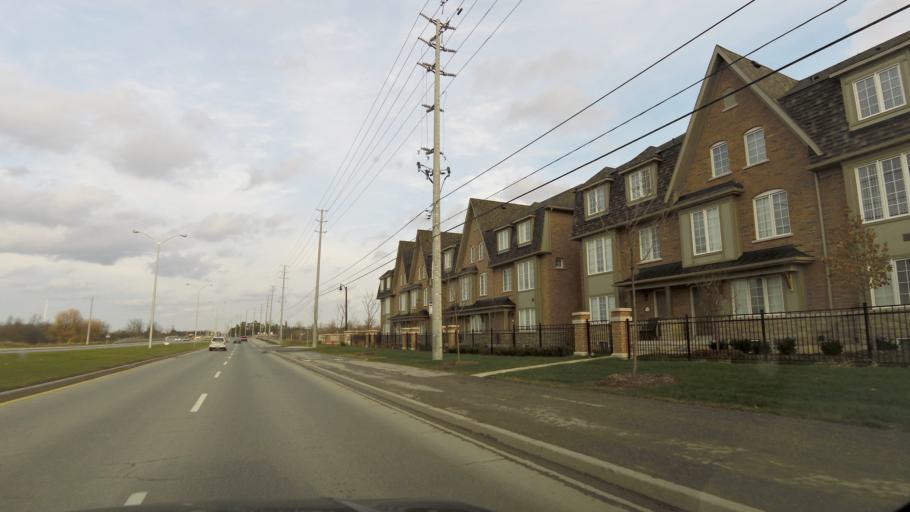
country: CA
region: Ontario
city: Brampton
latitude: 43.7832
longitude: -79.6993
